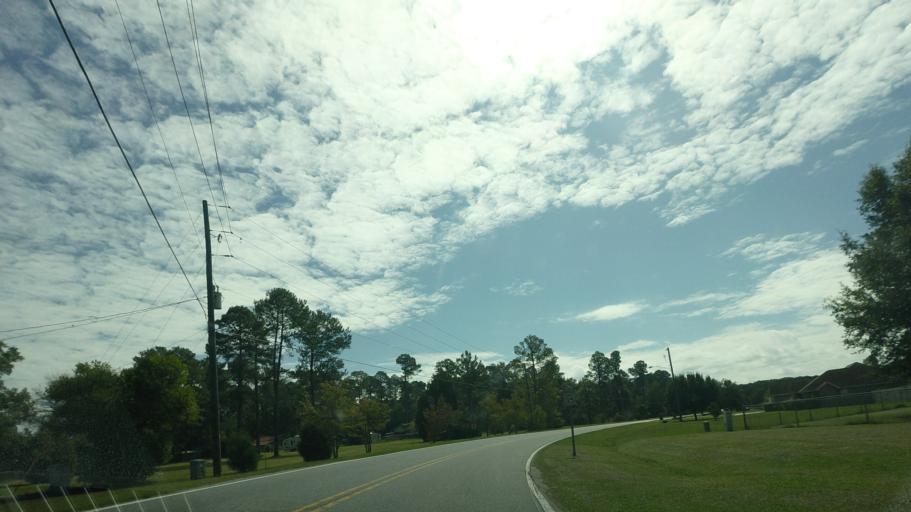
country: US
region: Georgia
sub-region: Houston County
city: Centerville
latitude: 32.5940
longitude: -83.7082
